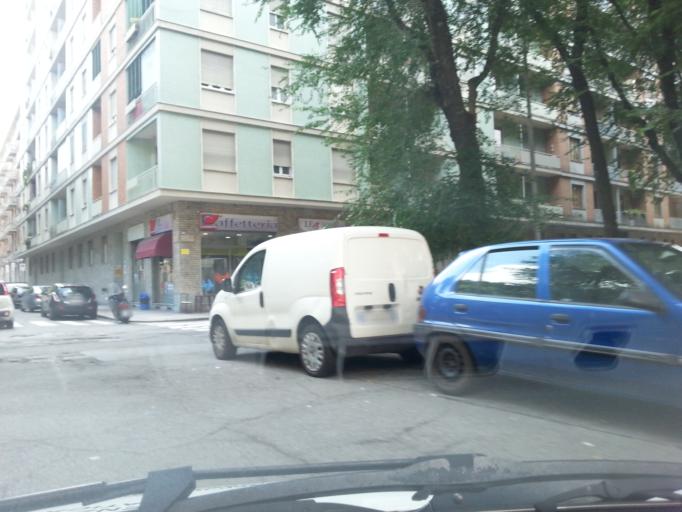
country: IT
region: Piedmont
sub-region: Provincia di Torino
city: Turin
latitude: 45.0833
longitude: 7.6778
